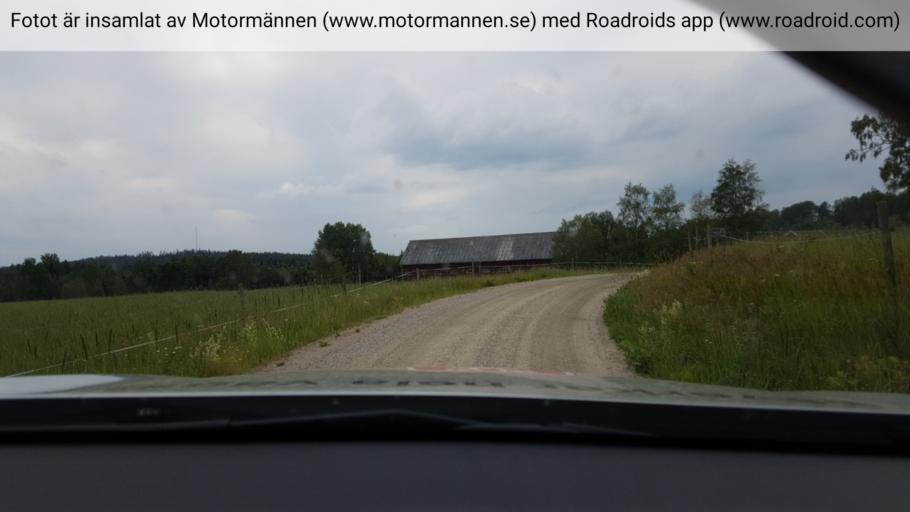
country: SE
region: Joenkoeping
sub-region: Mullsjo Kommun
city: Mullsjoe
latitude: 57.9152
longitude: 13.6935
